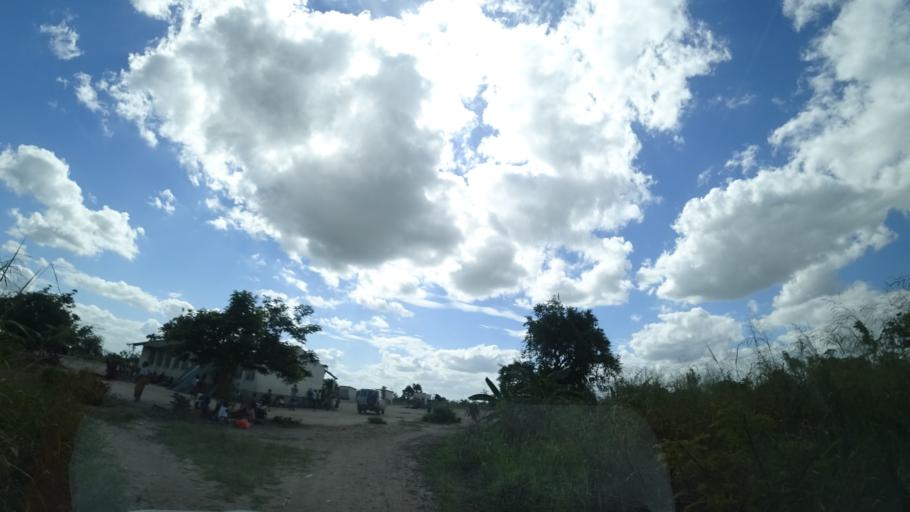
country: MZ
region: Sofala
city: Dondo
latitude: -19.3370
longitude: 34.5824
